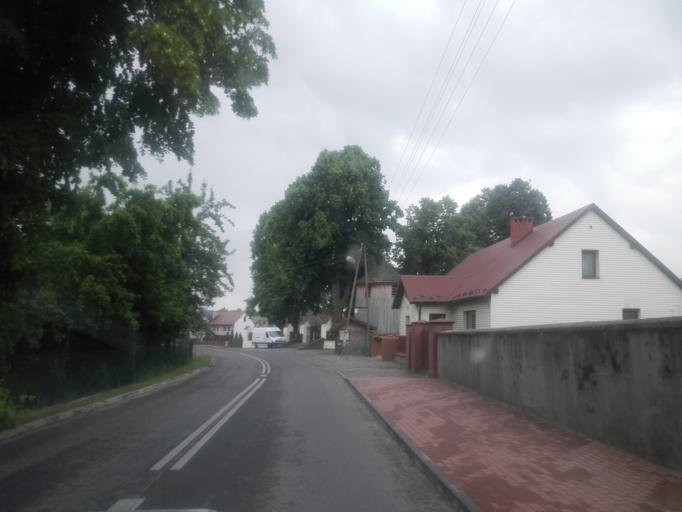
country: PL
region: Silesian Voivodeship
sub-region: Powiat czestochowski
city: Olsztyn
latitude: 50.7218
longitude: 19.3292
